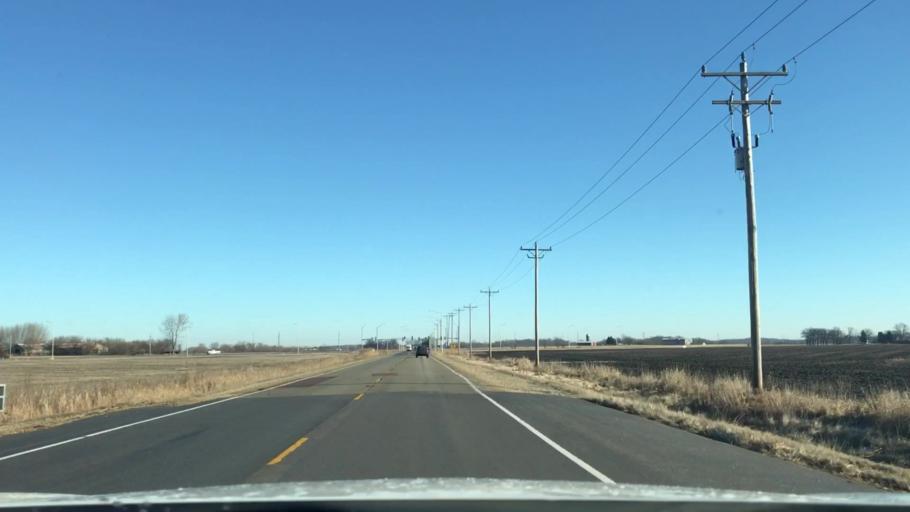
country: US
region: Illinois
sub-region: Kane County
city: Pingree Grove
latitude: 42.1083
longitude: -88.4494
